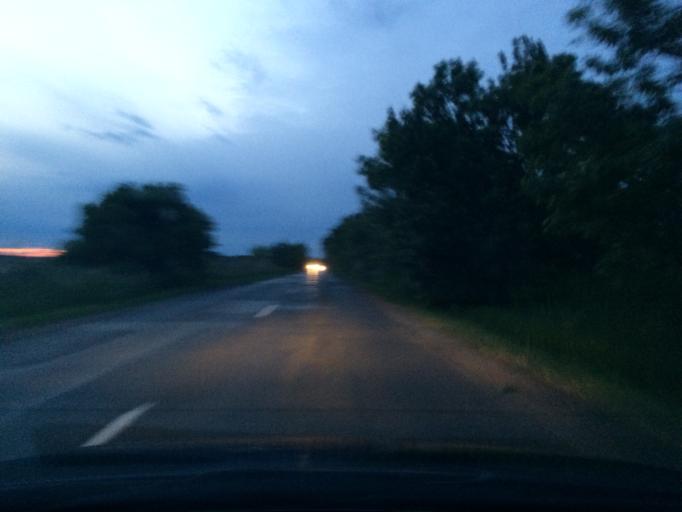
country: HU
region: Hajdu-Bihar
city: Hajdunanas
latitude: 47.8910
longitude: 21.4118
